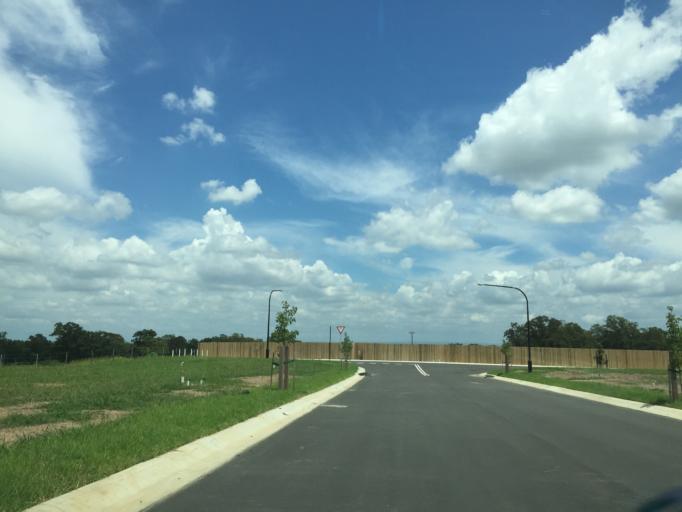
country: AU
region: New South Wales
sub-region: Blacktown
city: Riverstone
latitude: -33.6999
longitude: 150.8866
